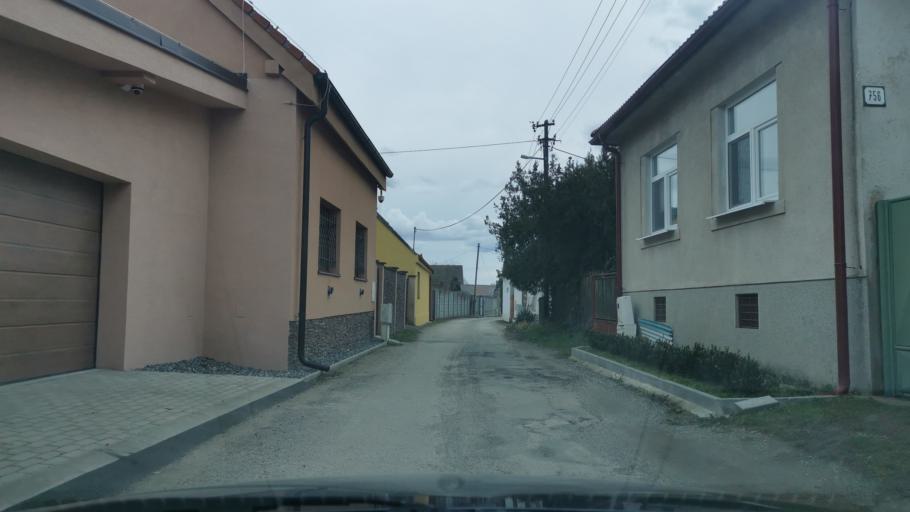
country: CZ
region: South Moravian
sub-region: Okres Breclav
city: Lanzhot
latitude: 48.6904
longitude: 17.0041
